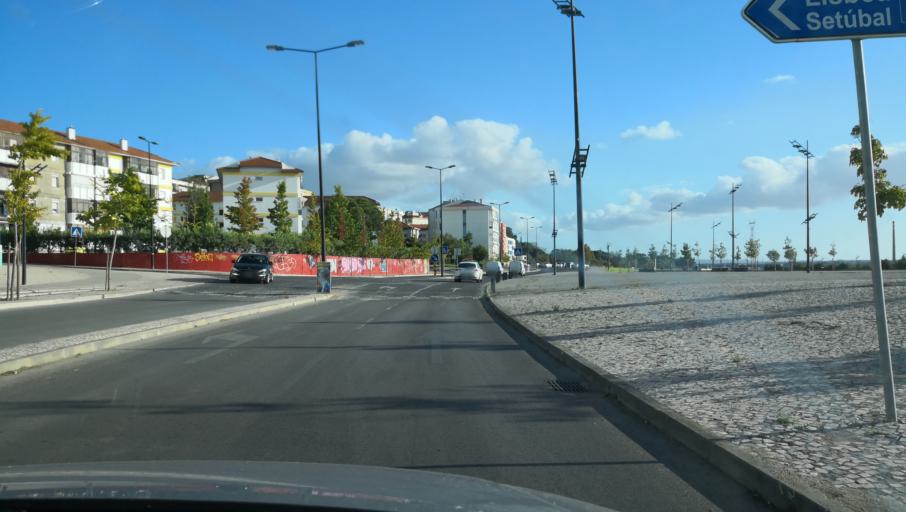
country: PT
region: Setubal
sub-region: Barreiro
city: Barreiro
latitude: 38.6486
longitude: -9.0651
